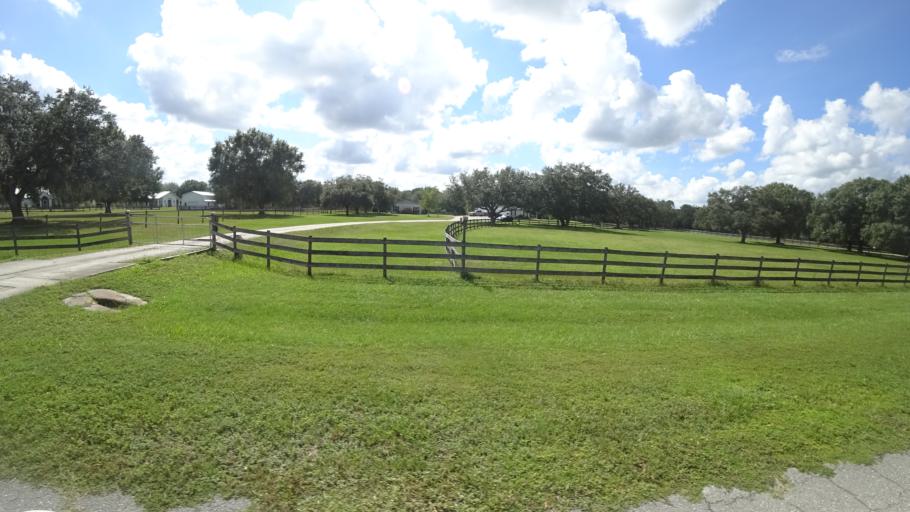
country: US
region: Florida
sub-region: Sarasota County
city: Lake Sarasota
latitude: 27.2799
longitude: -82.2235
